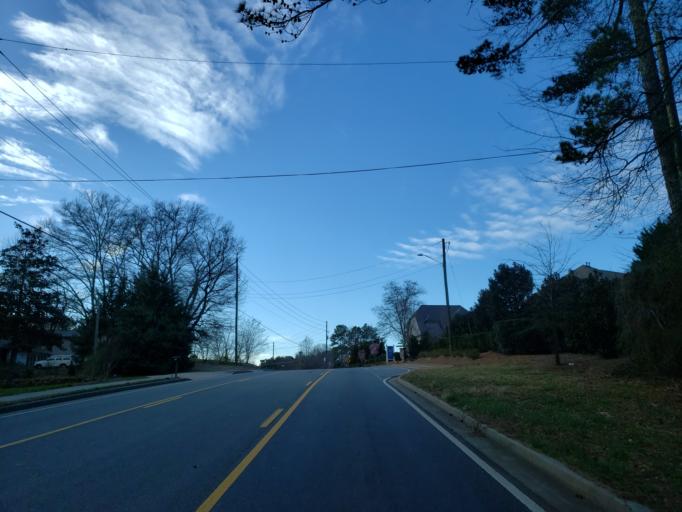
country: US
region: Georgia
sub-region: Cherokee County
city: Woodstock
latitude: 34.0695
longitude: -84.5456
